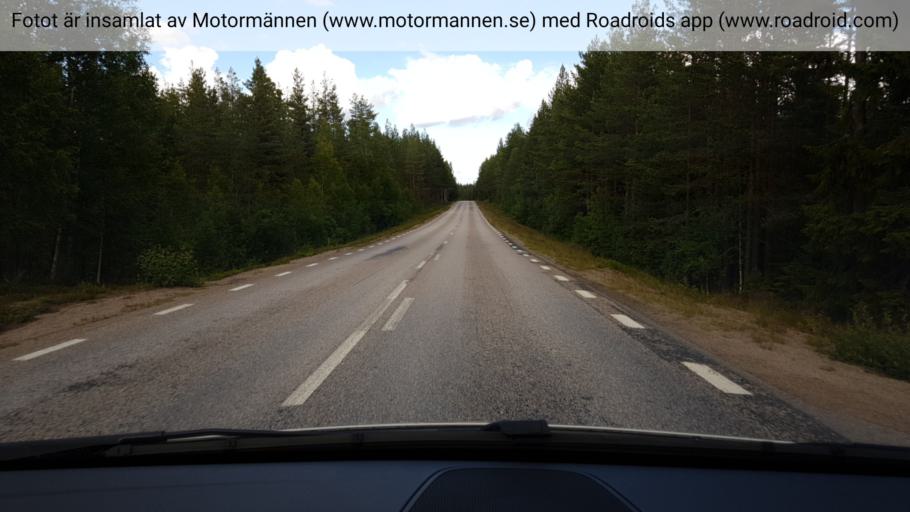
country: SE
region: Gaevleborg
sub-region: Ljusdals Kommun
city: Farila
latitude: 61.9808
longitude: 15.1274
